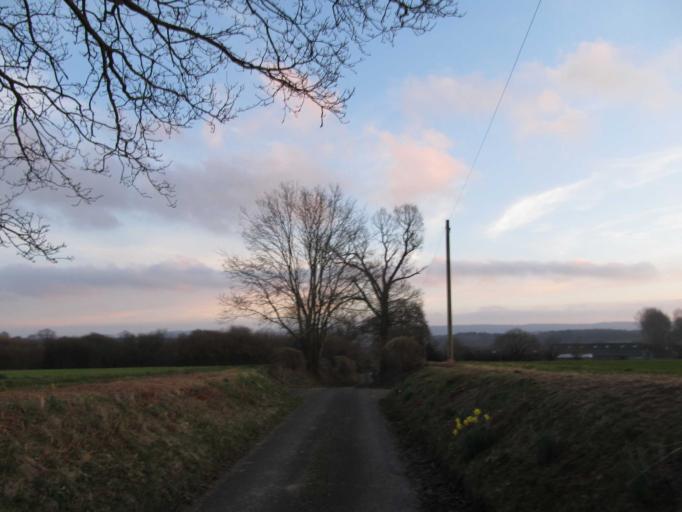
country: GB
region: England
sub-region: West Sussex
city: Petworth
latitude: 50.9874
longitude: -0.6585
